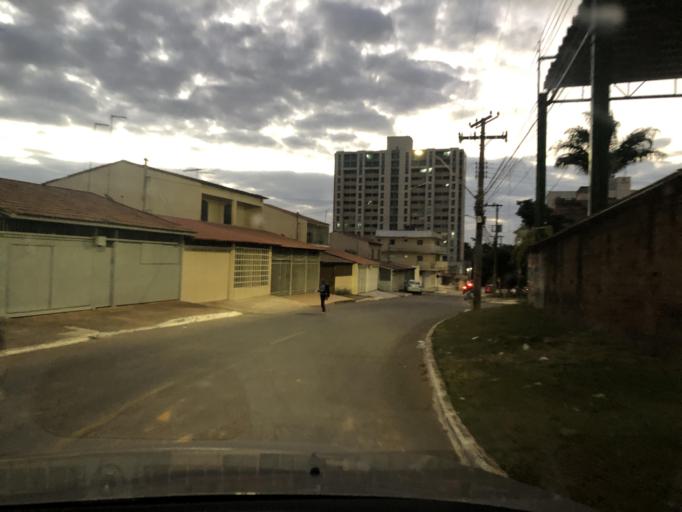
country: BR
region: Federal District
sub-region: Brasilia
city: Brasilia
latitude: -15.8522
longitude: -48.0733
